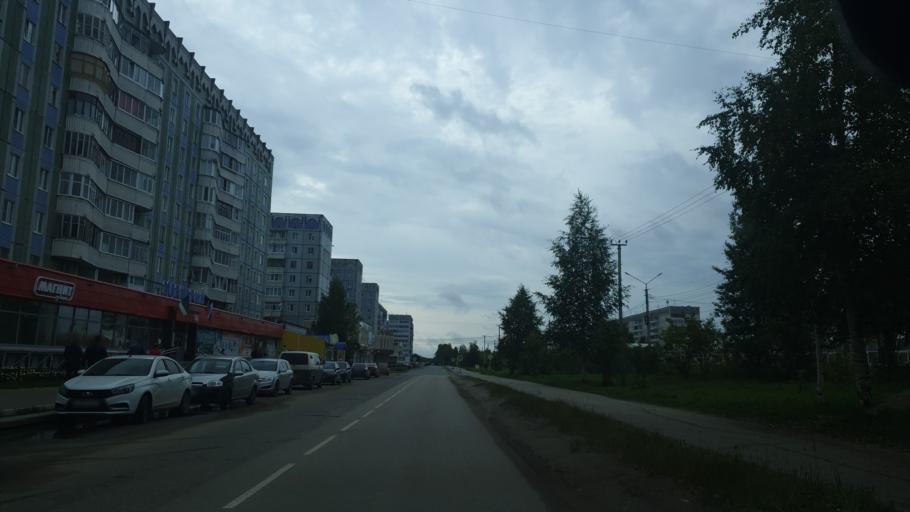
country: RU
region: Komi Republic
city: Ezhva
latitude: 61.7859
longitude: 50.7456
